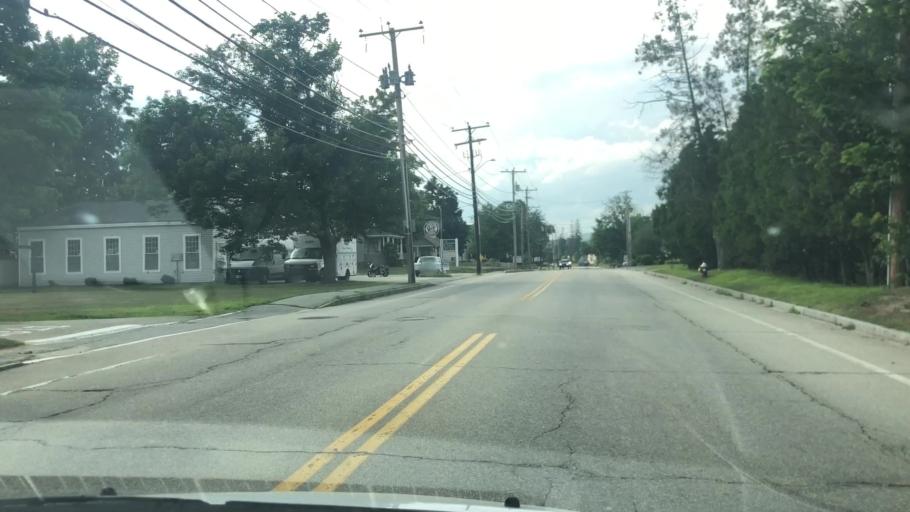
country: US
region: New Hampshire
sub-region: Hillsborough County
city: Milford
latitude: 42.8257
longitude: -71.6304
